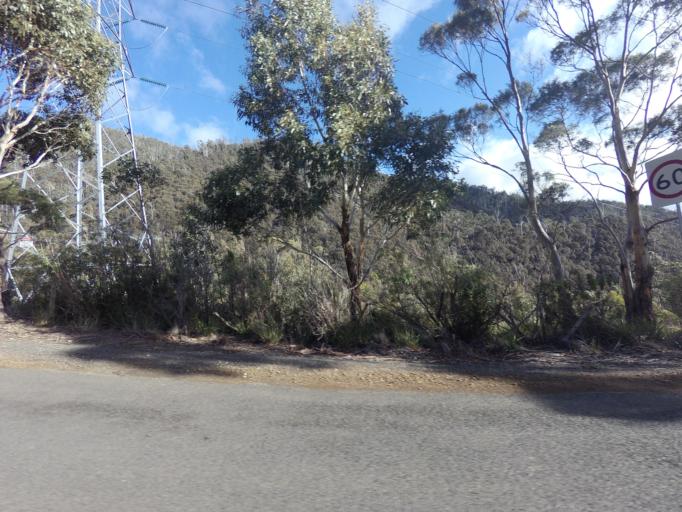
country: AU
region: Tasmania
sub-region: Glenorchy
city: Berriedale
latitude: -42.8165
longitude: 147.1761
